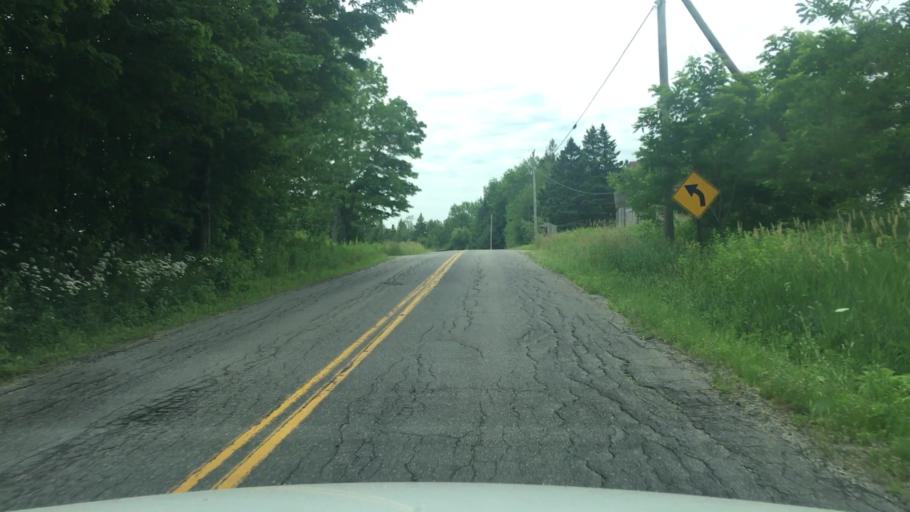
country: US
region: Maine
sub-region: Kennebec County
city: Albion
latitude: 44.4928
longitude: -69.3739
